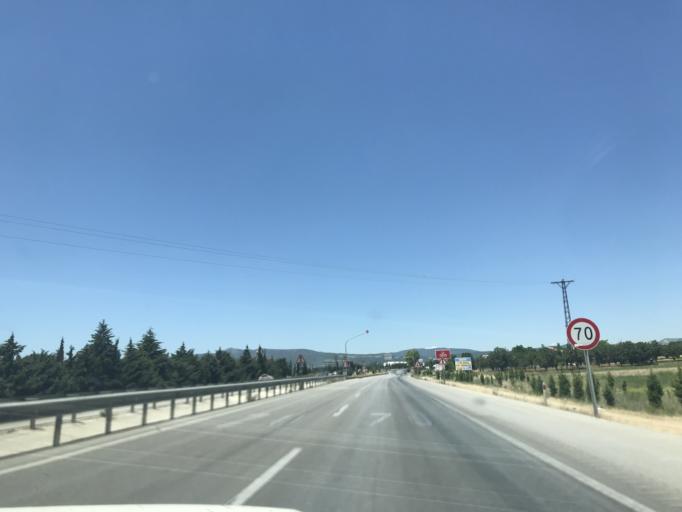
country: TR
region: Isparta
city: Gonen
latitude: 37.8910
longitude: 30.4128
